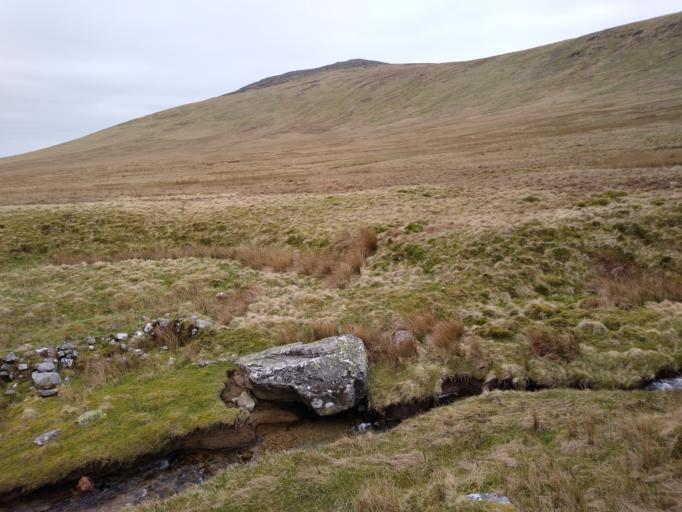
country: GB
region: England
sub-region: Cumbria
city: Keswick
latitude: 54.7051
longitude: -3.0356
